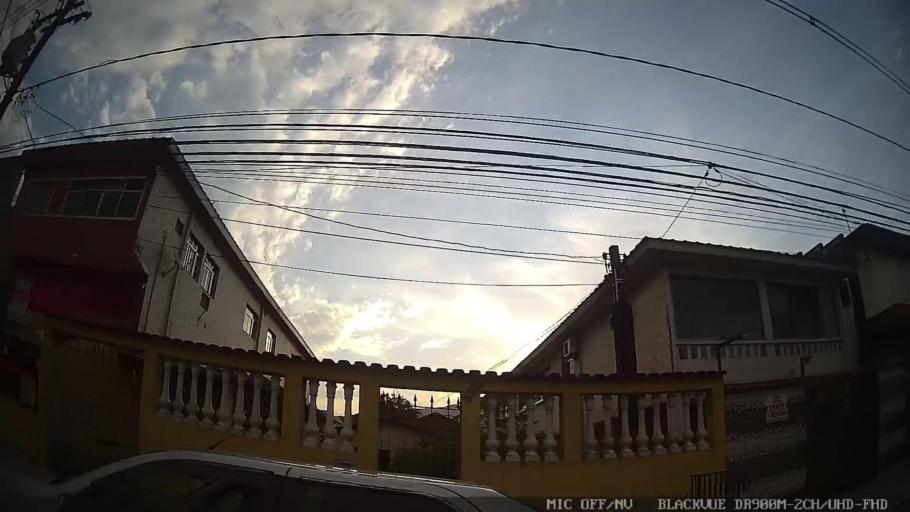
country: BR
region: Sao Paulo
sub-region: Cubatao
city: Cubatao
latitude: -23.8955
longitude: -46.4212
